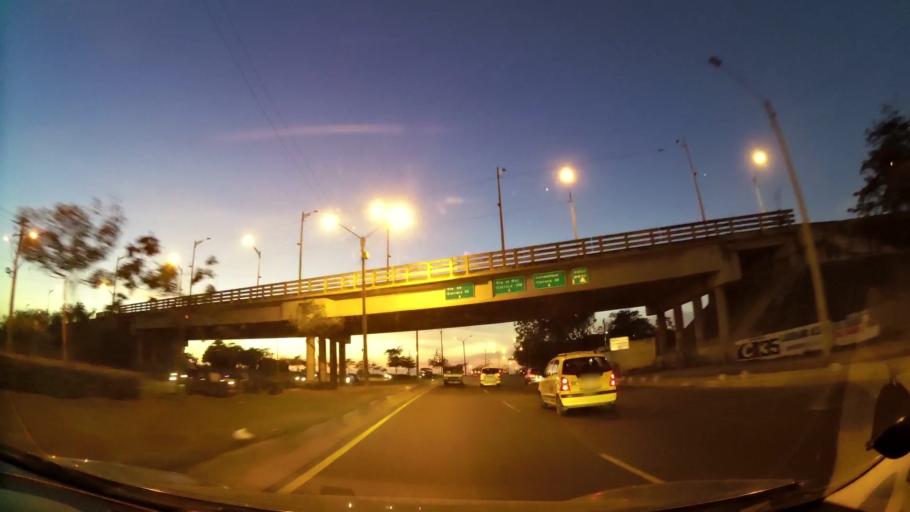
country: CO
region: Atlantico
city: Soledad
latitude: 10.9227
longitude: -74.8161
